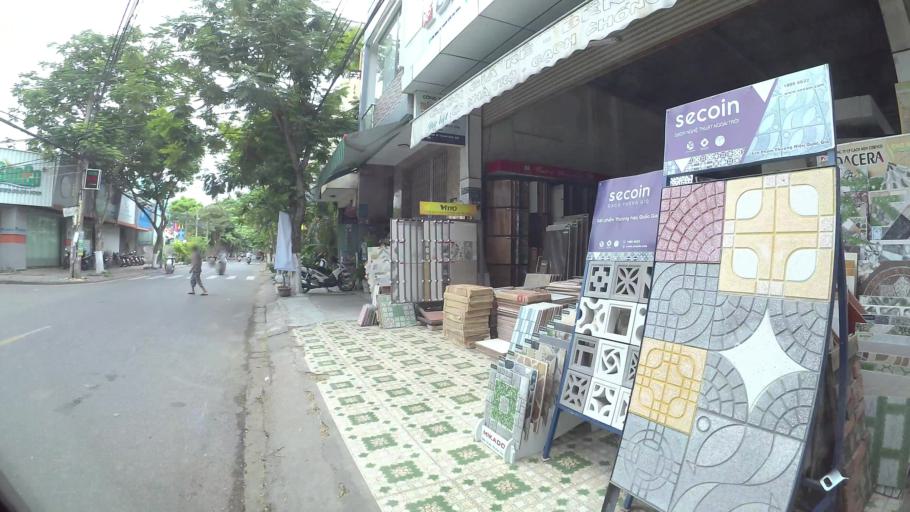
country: VN
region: Da Nang
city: Thanh Khe
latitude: 16.0747
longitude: 108.1750
